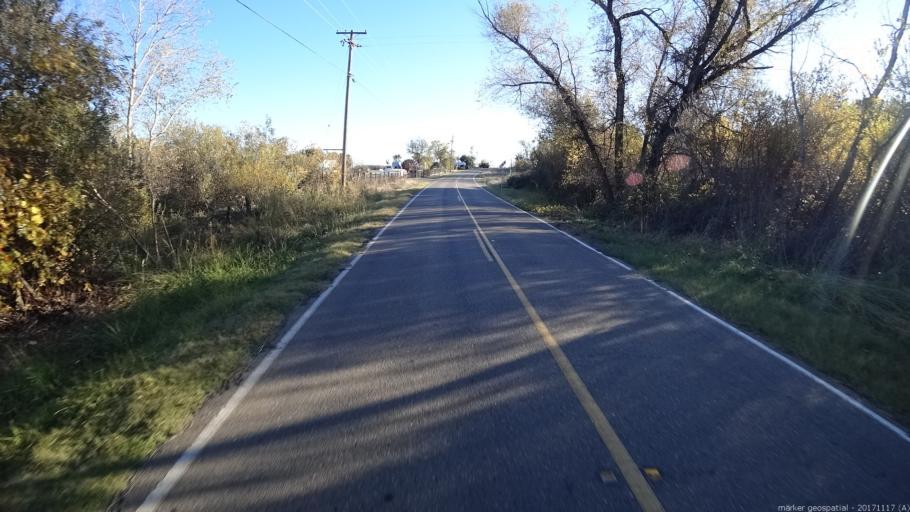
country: US
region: California
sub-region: Shasta County
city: Cottonwood
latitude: 40.4074
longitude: -122.2446
